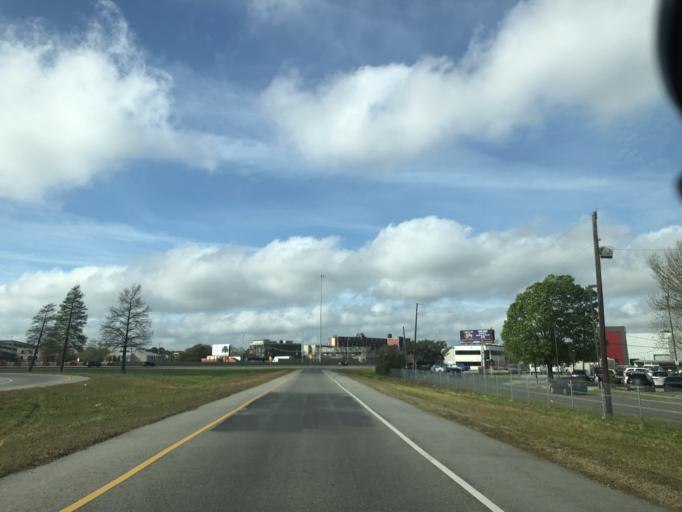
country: US
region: Louisiana
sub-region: Jefferson Parish
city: Metairie Terrace
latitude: 30.0010
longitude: -90.1859
